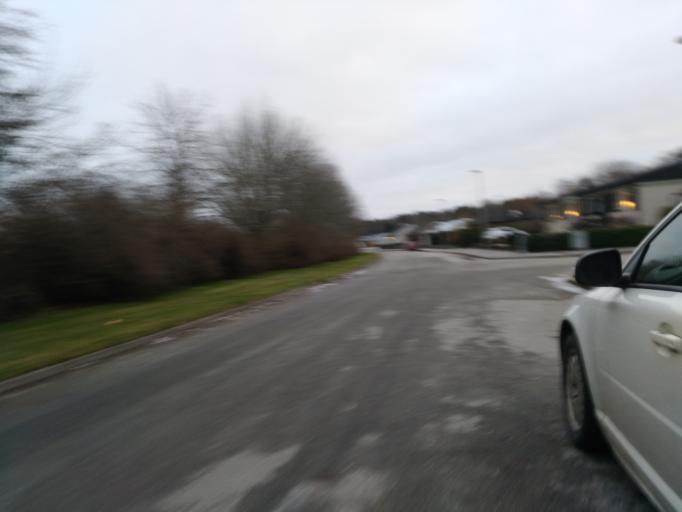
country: SE
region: Vaestra Goetaland
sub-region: Lidkopings Kommun
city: Lidkoping
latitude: 58.4932
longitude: 13.1659
